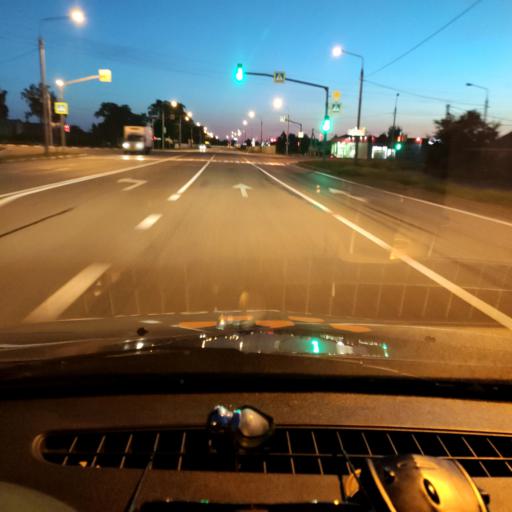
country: RU
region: Belgorod
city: Skorodnoye
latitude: 51.1866
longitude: 37.3743
